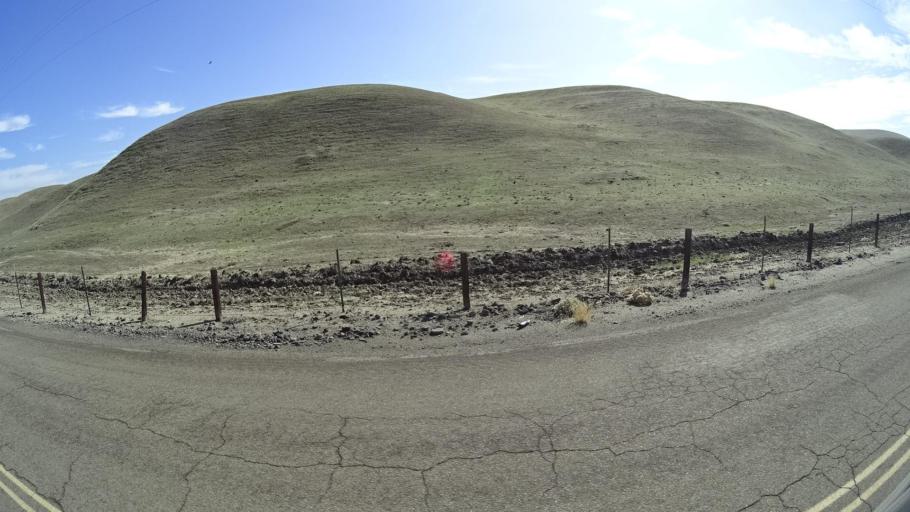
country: US
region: California
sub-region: Tulare County
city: Richgrove
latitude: 35.6362
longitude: -118.9459
